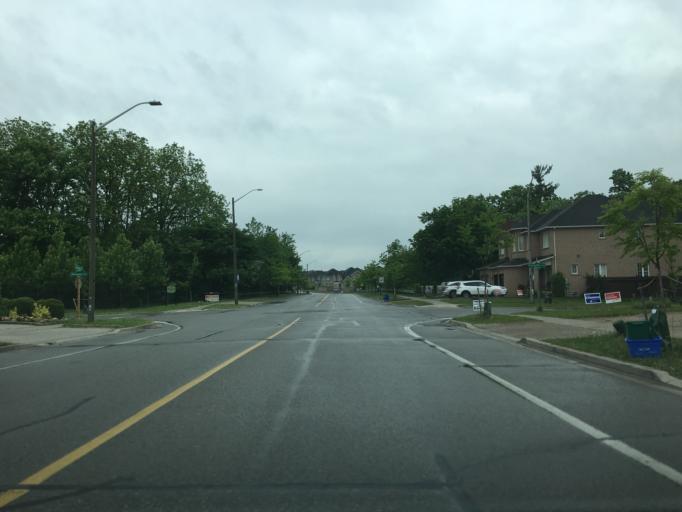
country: CA
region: Ontario
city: Markham
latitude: 43.8395
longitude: -79.2461
